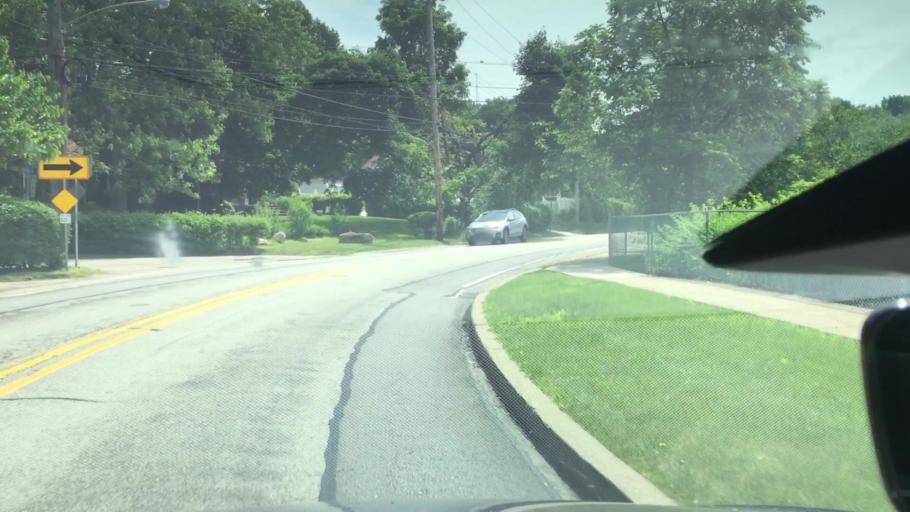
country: US
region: Pennsylvania
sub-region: Allegheny County
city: Penn Hills
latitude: 40.4805
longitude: -79.8360
